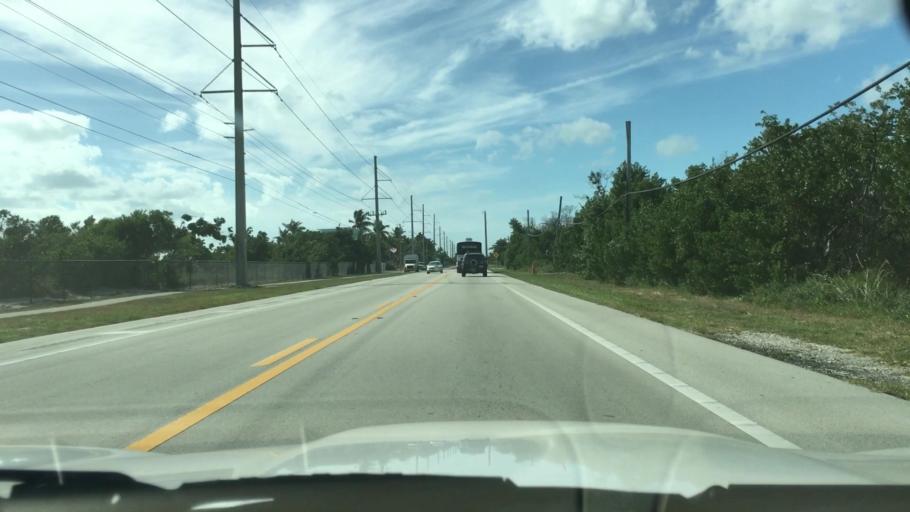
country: US
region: Florida
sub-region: Monroe County
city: Islamorada
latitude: 24.8067
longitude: -80.8405
